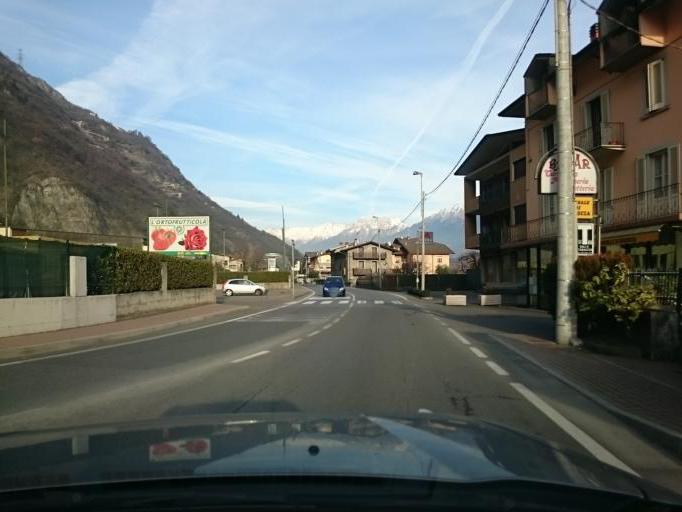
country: IT
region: Lombardy
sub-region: Provincia di Brescia
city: Piamborno
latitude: 45.9203
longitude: 10.2260
